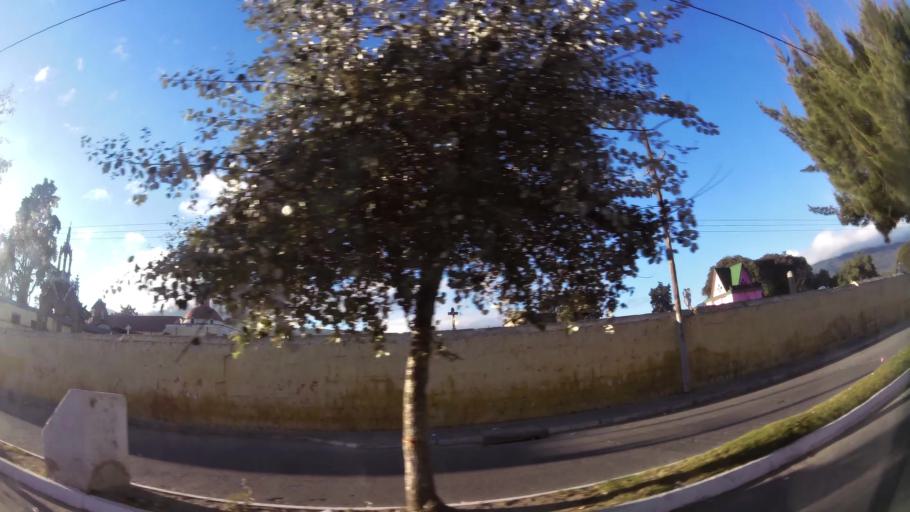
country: GT
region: Quetzaltenango
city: Quetzaltenango
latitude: 14.8373
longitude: -91.5263
